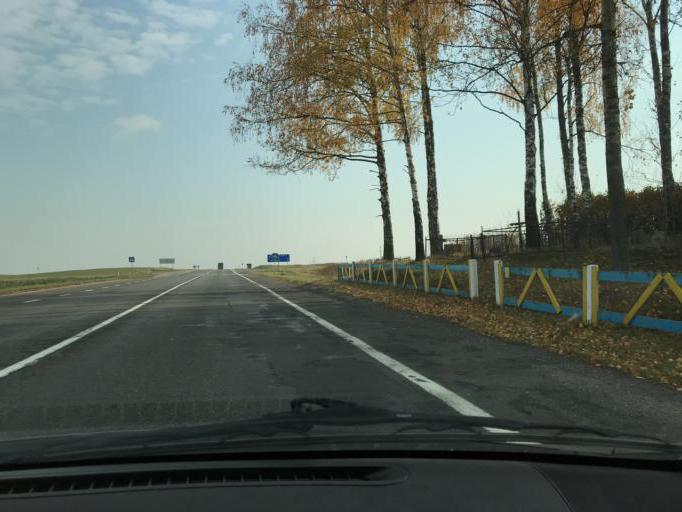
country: BY
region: Vitebsk
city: Chashniki
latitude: 55.0131
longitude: 29.0622
